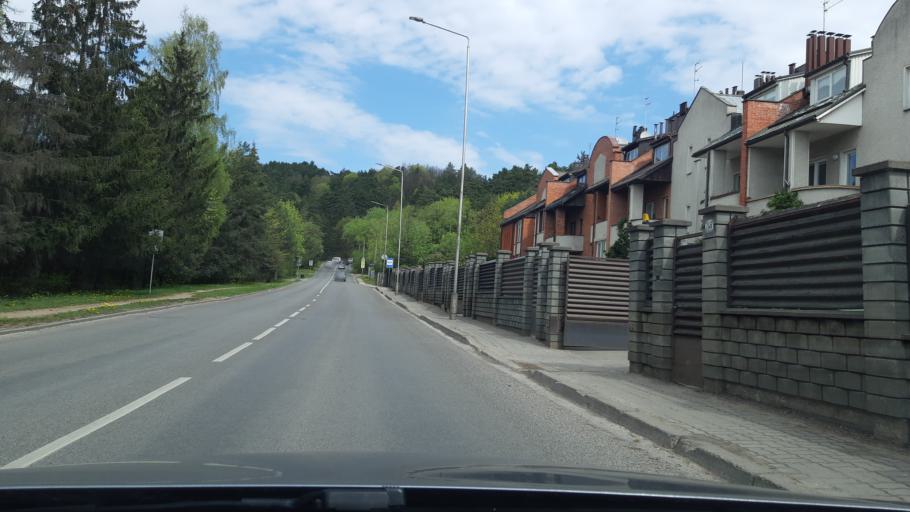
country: LT
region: Kauno apskritis
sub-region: Kauno rajonas
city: Akademija (Kaunas)
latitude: 54.9209
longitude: 23.8271
